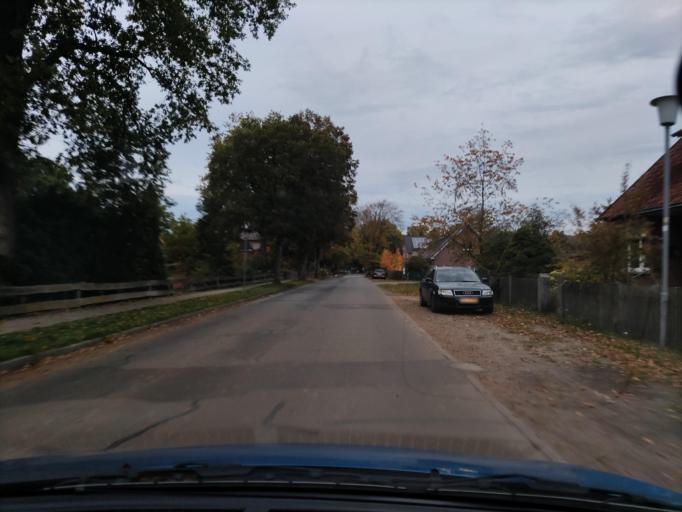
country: DE
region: Lower Saxony
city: Hermannsburg
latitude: 52.8735
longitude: 10.1209
